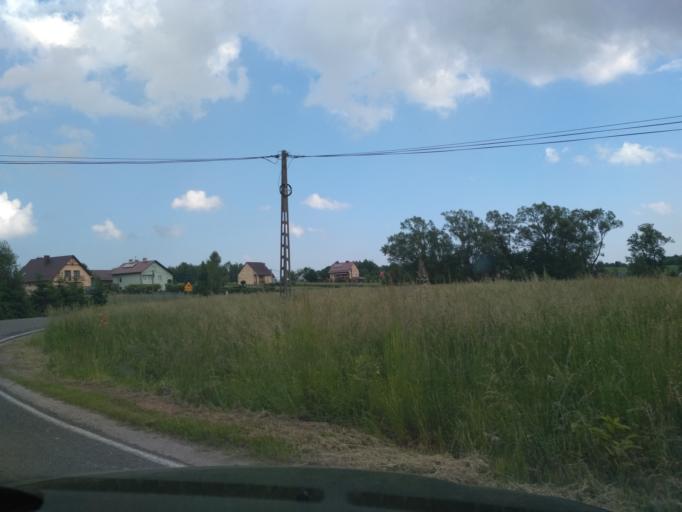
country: PL
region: Subcarpathian Voivodeship
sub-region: Powiat rzeszowski
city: Hyzne
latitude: 49.9320
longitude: 22.1858
